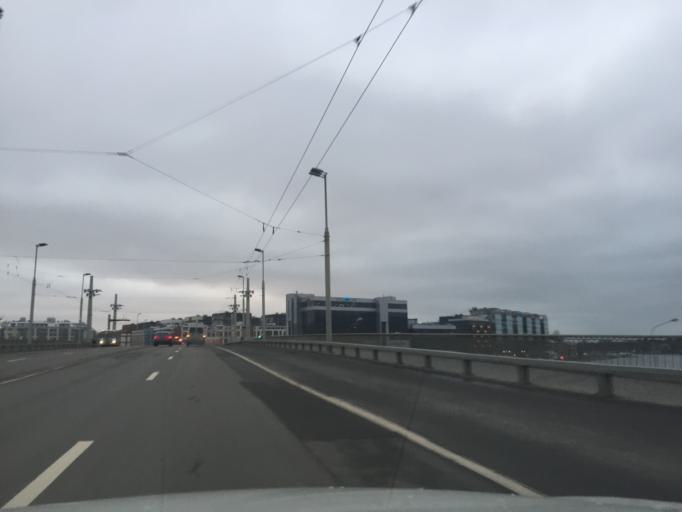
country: RU
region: St.-Petersburg
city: Petrogradka
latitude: 59.9795
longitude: 30.3236
